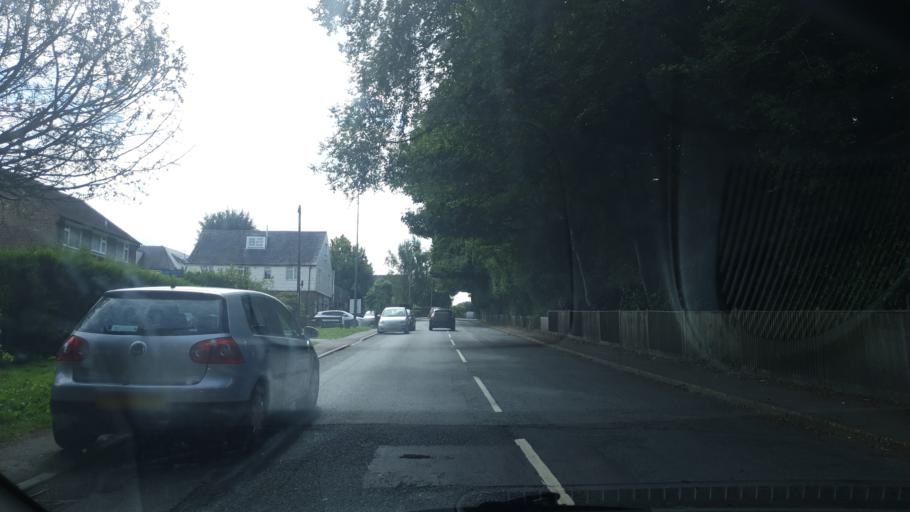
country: GB
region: England
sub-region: East Sussex
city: Forest Row
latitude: 51.0964
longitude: 0.0336
